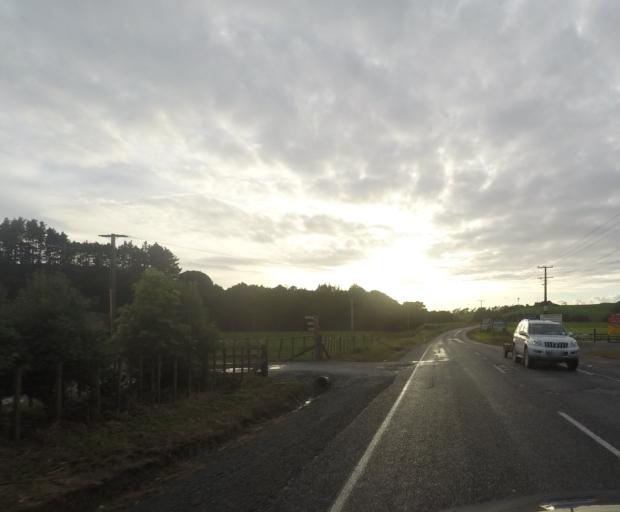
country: NZ
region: Auckland
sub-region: Auckland
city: Wellsford
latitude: -36.2206
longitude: 174.5784
